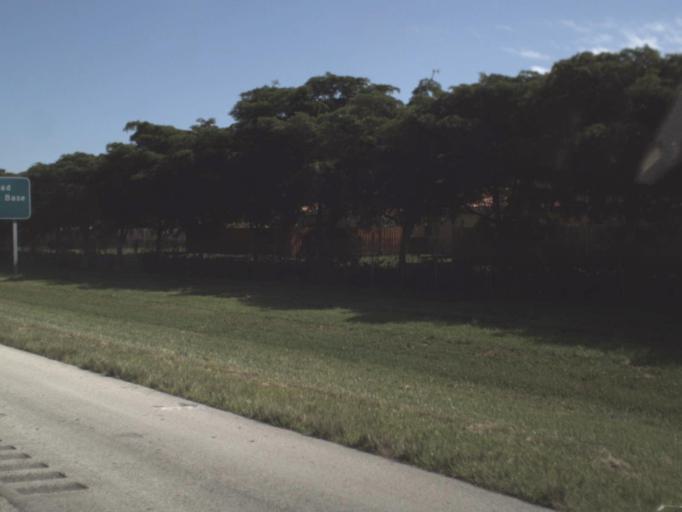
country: US
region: Florida
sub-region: Miami-Dade County
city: Leisure City
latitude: 25.4879
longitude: -80.4242
